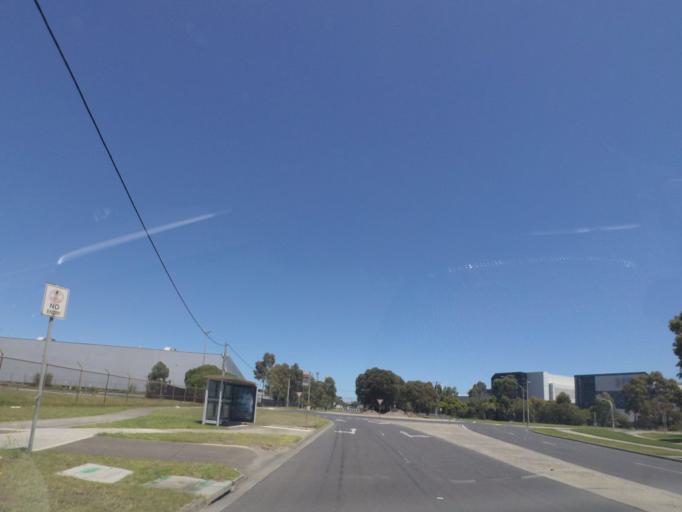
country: AU
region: Victoria
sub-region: Maribyrnong
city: Yarraville
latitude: -37.8261
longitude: 144.9117
